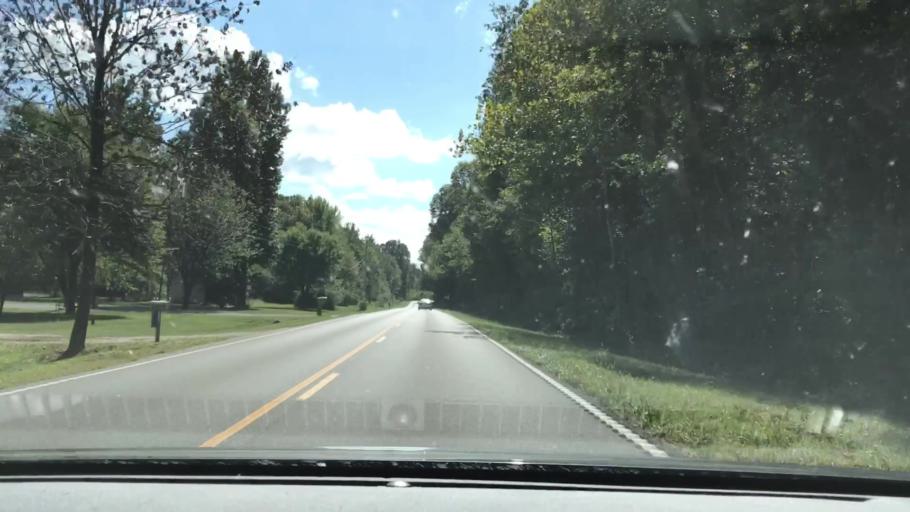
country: US
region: Kentucky
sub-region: McCracken County
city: Reidland
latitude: 36.9670
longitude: -88.5151
